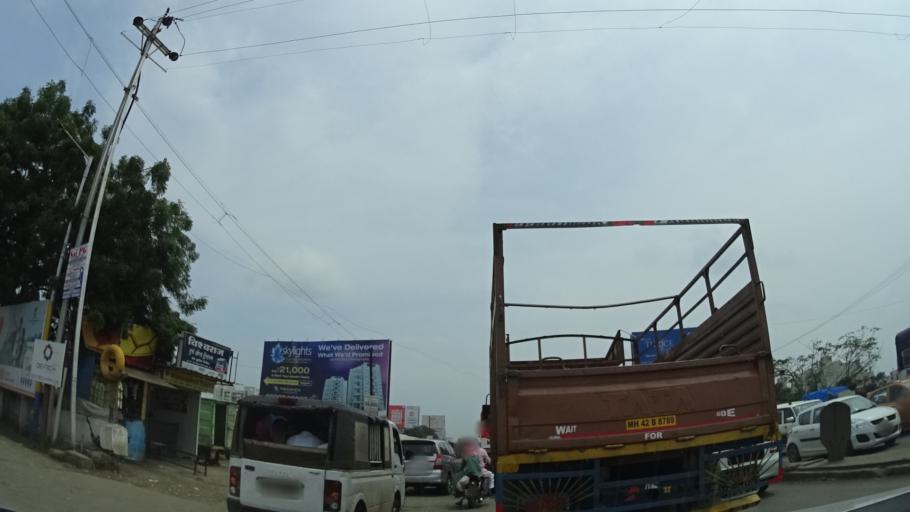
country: IN
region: Maharashtra
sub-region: Pune Division
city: Lohogaon
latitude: 18.5821
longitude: 73.9876
